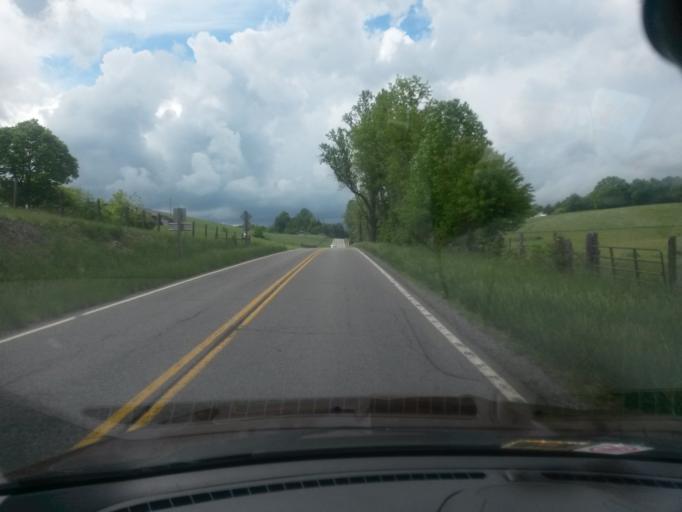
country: US
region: Virginia
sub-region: Floyd County
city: Floyd
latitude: 36.8609
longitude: -80.3246
